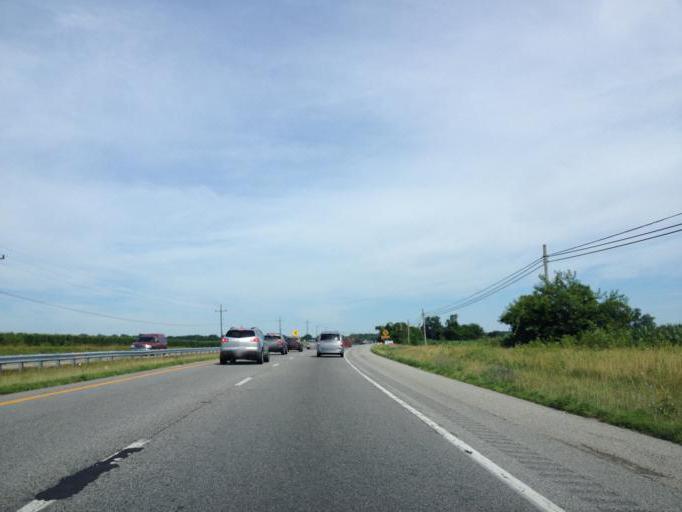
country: US
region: Maryland
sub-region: Queen Anne's County
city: Centreville
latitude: 38.9673
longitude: -76.1160
